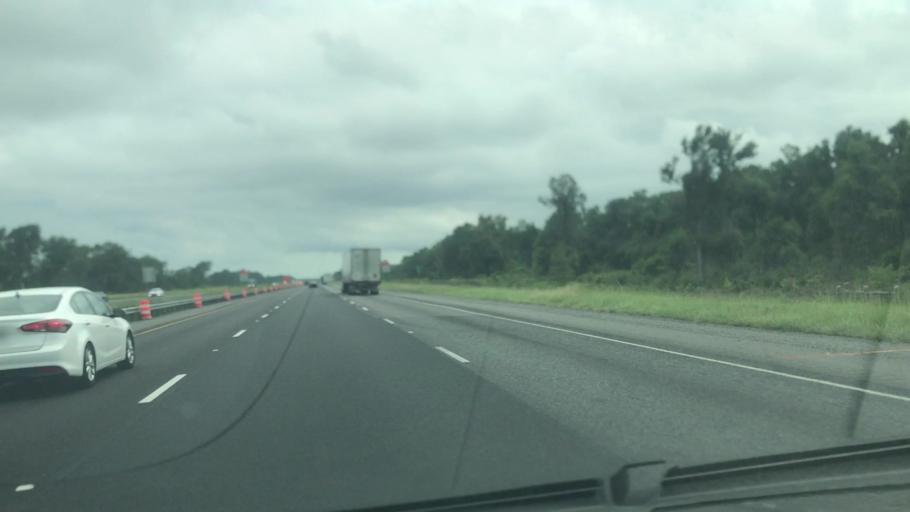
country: US
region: Georgia
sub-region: Camden County
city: Woodbine
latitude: 31.0255
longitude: -81.6566
